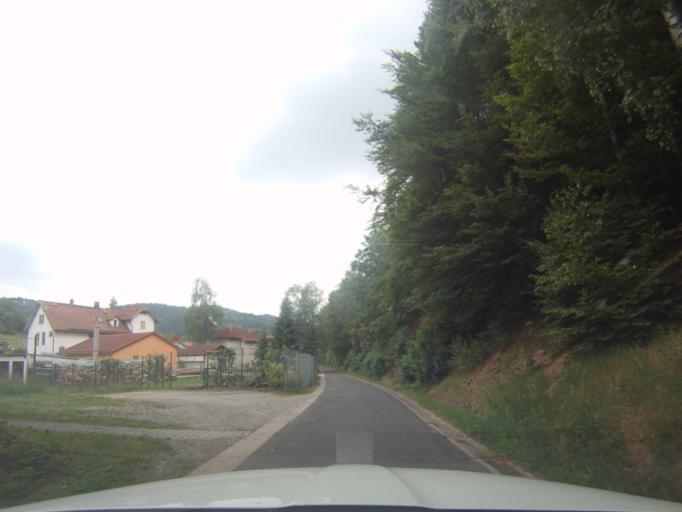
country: DE
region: Thuringia
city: Frauenwald
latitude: 50.5231
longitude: 10.8772
